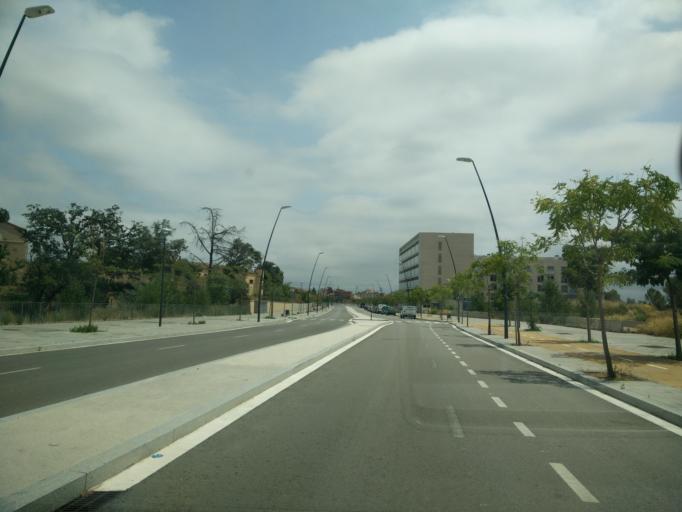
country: ES
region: Catalonia
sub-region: Provincia de Barcelona
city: Terrassa
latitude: 41.5821
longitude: 1.9970
